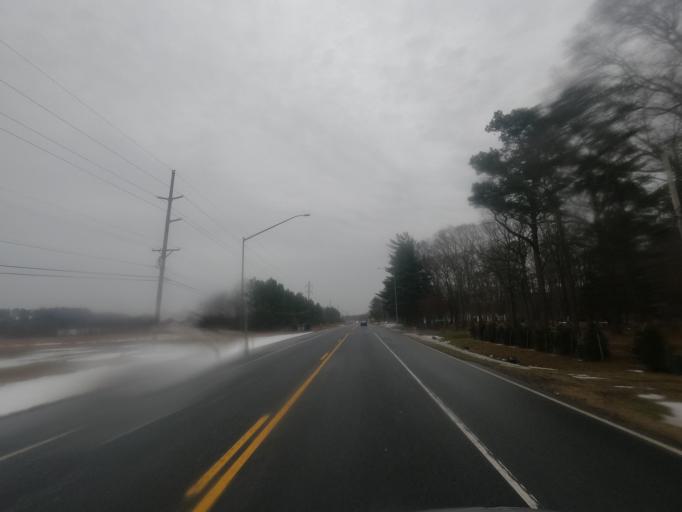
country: US
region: Maryland
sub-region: Dorchester County
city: Cambridge
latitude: 38.5599
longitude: -75.9971
